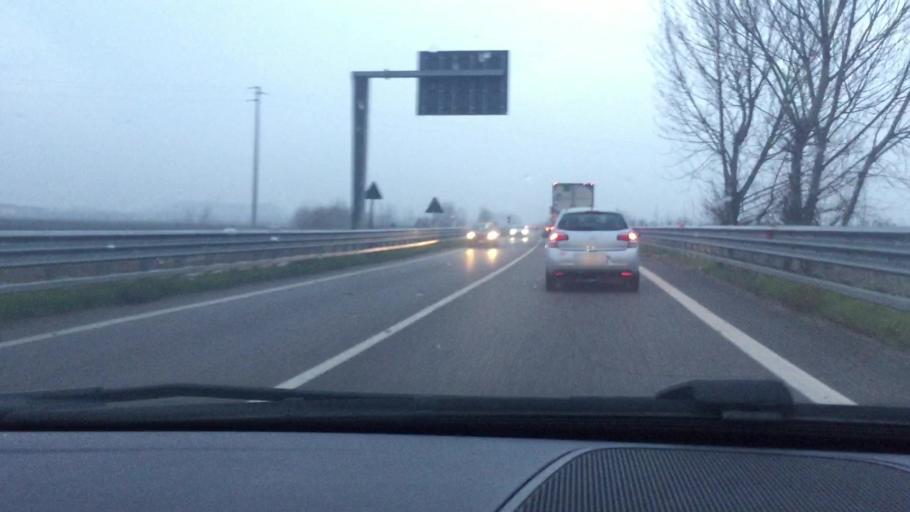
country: IT
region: Veneto
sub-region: Provincia di Venezia
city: Campolongo Maggiore
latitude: 45.3167
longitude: 12.0336
